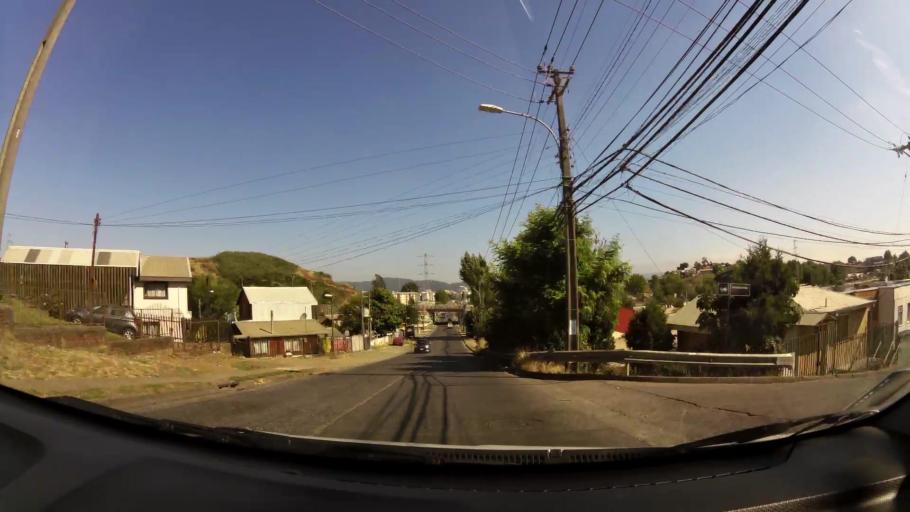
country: CL
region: Biobio
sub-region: Provincia de Concepcion
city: Concepcion
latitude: -36.7974
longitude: -73.0489
